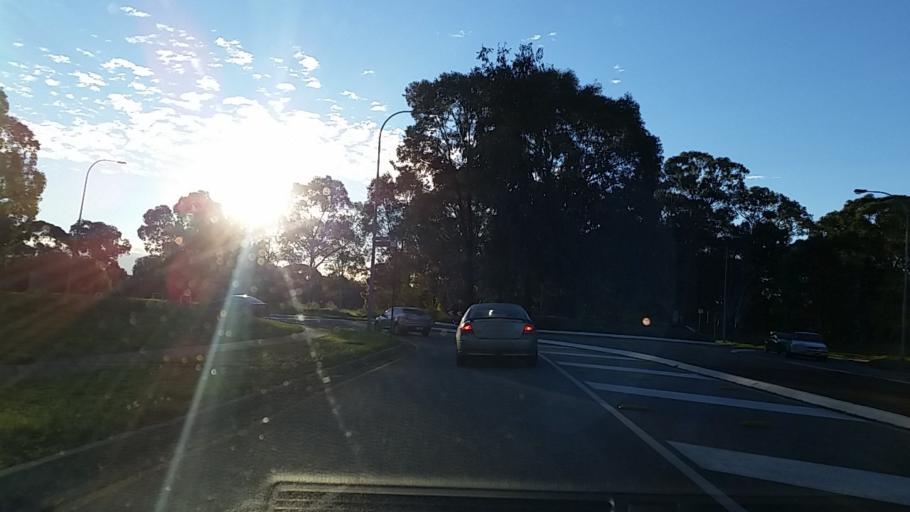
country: AU
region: South Australia
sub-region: Salisbury
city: Salisbury
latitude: -34.7480
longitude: 138.6394
